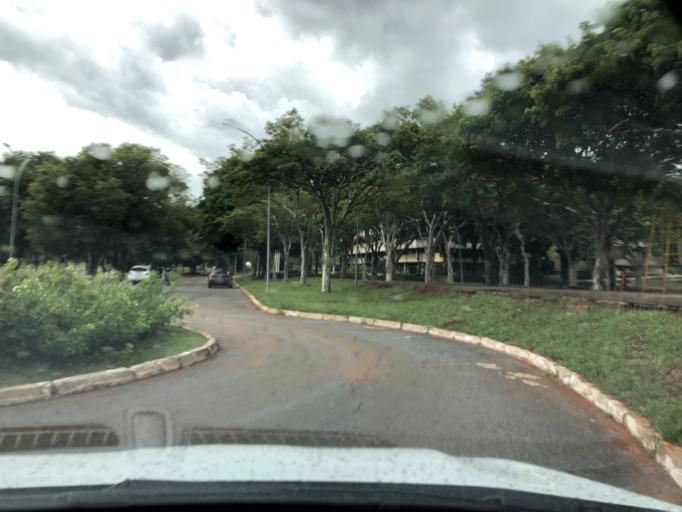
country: BR
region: Federal District
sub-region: Brasilia
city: Brasilia
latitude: -15.7617
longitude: -47.8673
